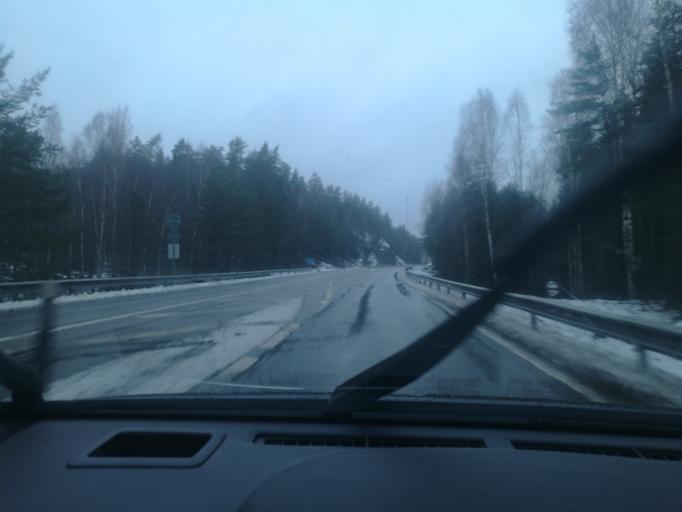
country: SE
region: OEstergoetland
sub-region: Norrkopings Kommun
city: Jursla
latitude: 58.7395
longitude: 16.1724
